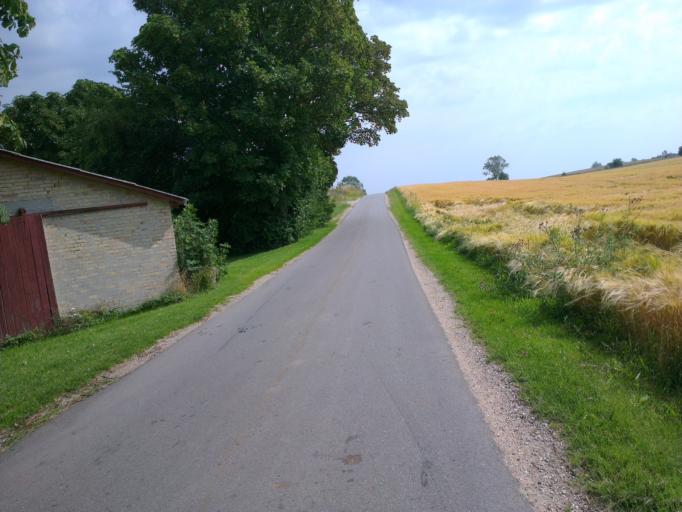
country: DK
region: Capital Region
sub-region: Frederikssund Kommune
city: Skibby
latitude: 55.7802
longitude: 11.9705
